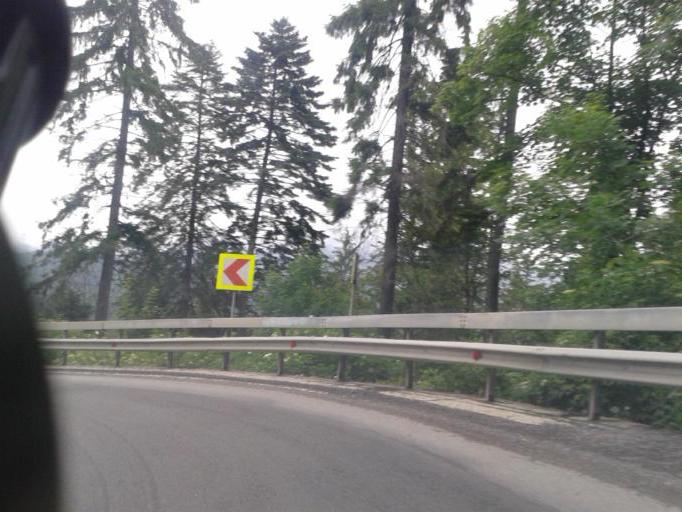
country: RO
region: Brasov
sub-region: Oras Predeal
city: Predeal
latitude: 45.5196
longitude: 25.5767
